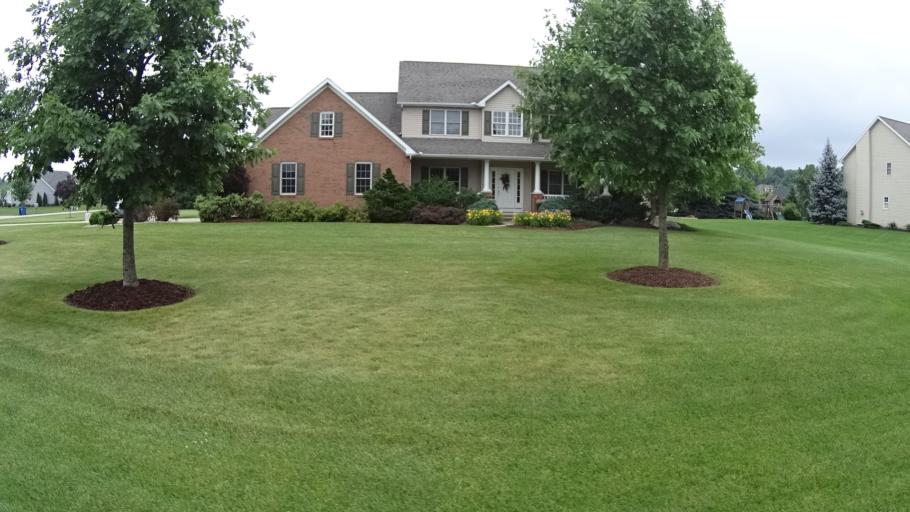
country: US
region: Ohio
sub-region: Erie County
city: Milan
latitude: 41.2962
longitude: -82.5837
